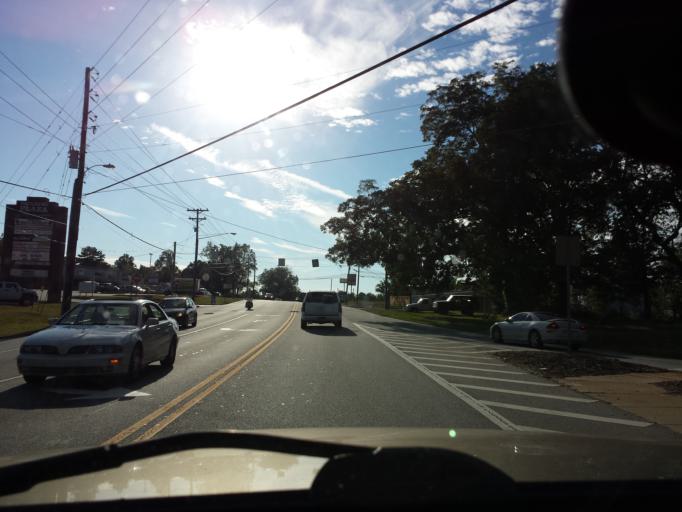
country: US
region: Georgia
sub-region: Paulding County
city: Dallas
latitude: 33.9106
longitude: -84.8037
